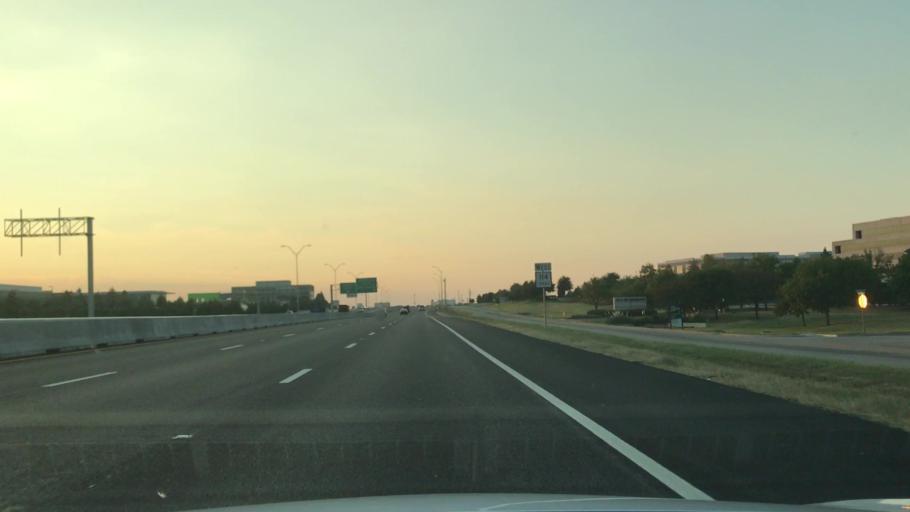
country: US
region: Texas
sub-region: Dallas County
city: Coppell
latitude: 32.8969
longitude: -96.9743
